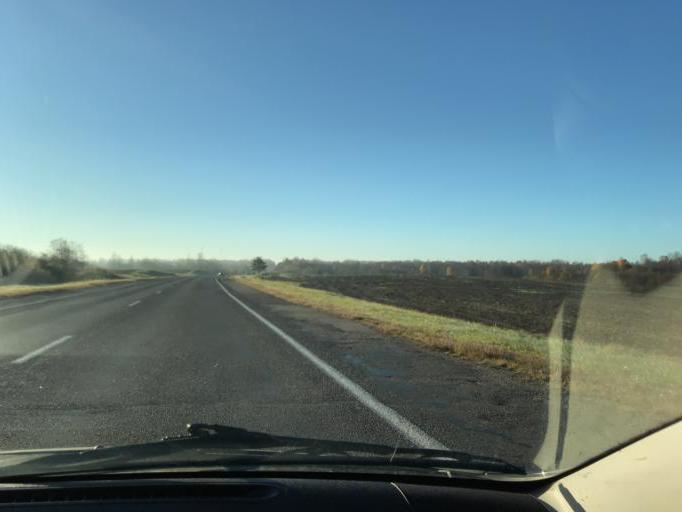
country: BY
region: Vitebsk
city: Vitebsk
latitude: 54.9263
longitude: 30.3734
